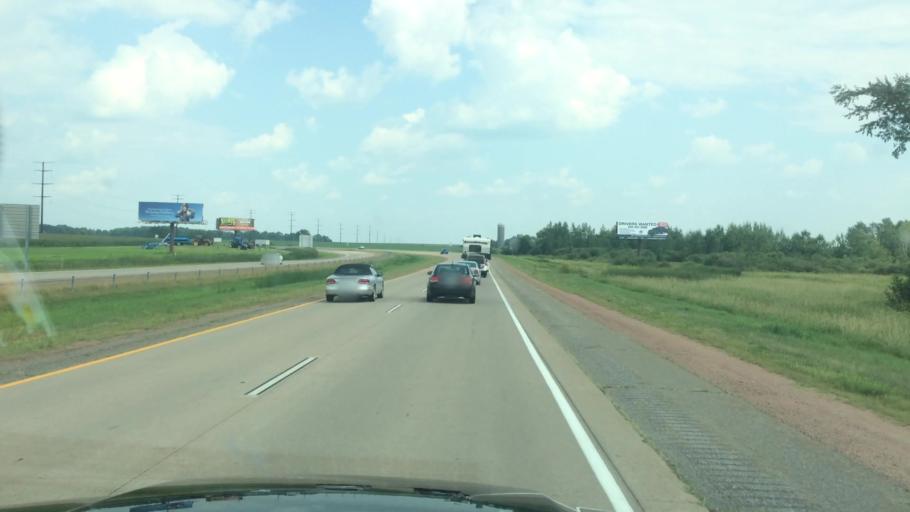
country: US
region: Wisconsin
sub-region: Clark County
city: Abbotsford
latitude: 44.9326
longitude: -90.3038
